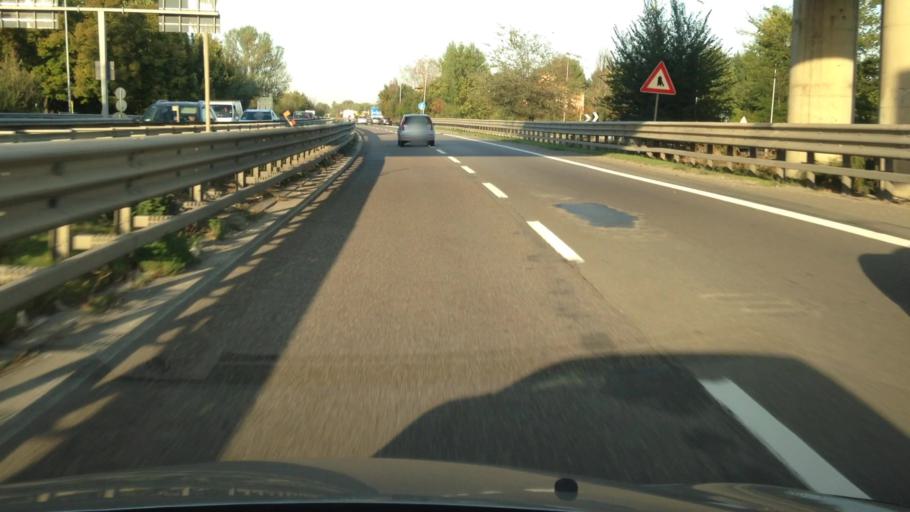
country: IT
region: Emilia-Romagna
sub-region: Provincia di Modena
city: Campogalliano
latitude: 44.6617
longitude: 10.8820
